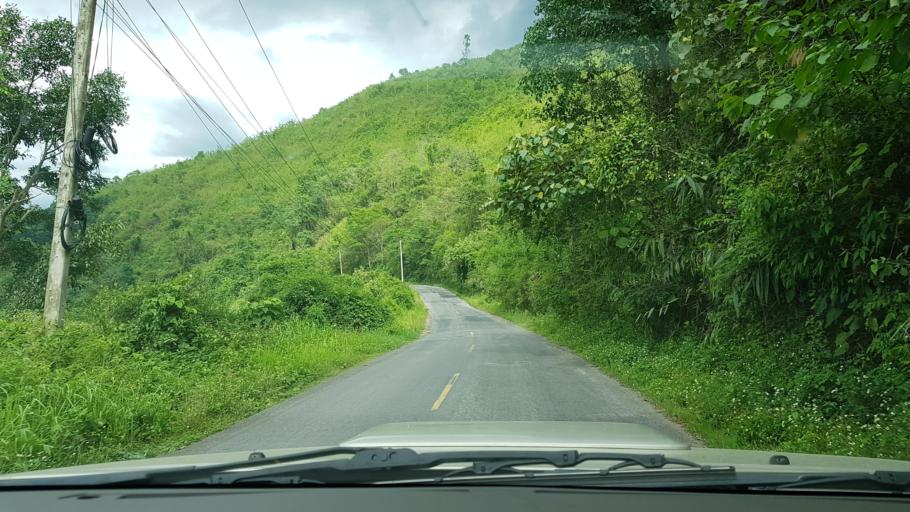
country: LA
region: Loungnamtha
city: Muang Nale
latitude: 20.3707
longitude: 101.7203
